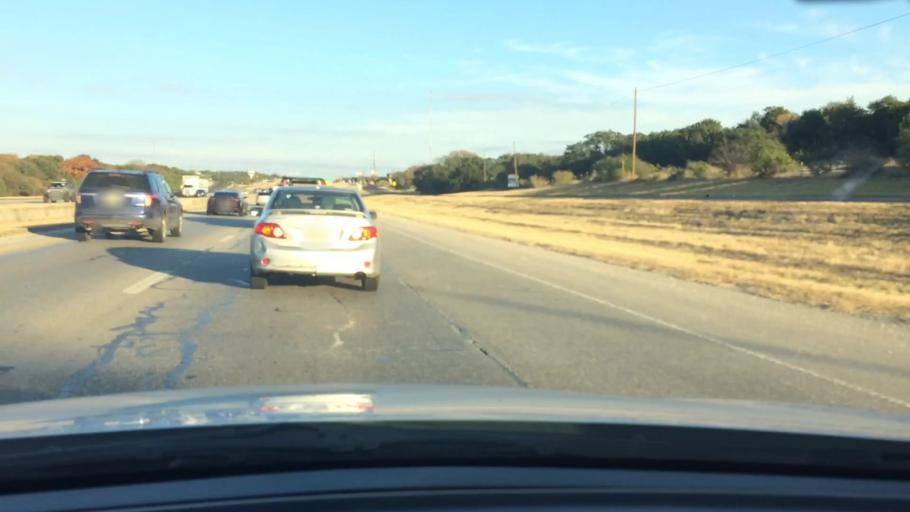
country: US
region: Texas
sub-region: Bexar County
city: Live Oak
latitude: 29.6019
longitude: -98.3989
